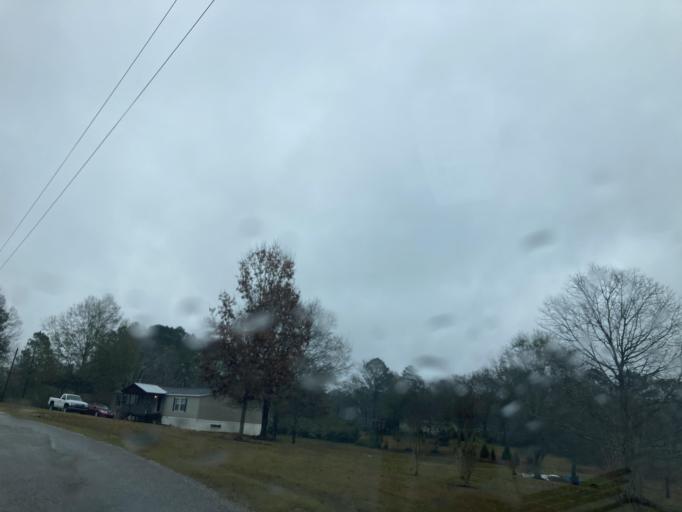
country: US
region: Mississippi
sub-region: Forrest County
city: Rawls Springs
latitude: 31.4822
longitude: -89.3849
